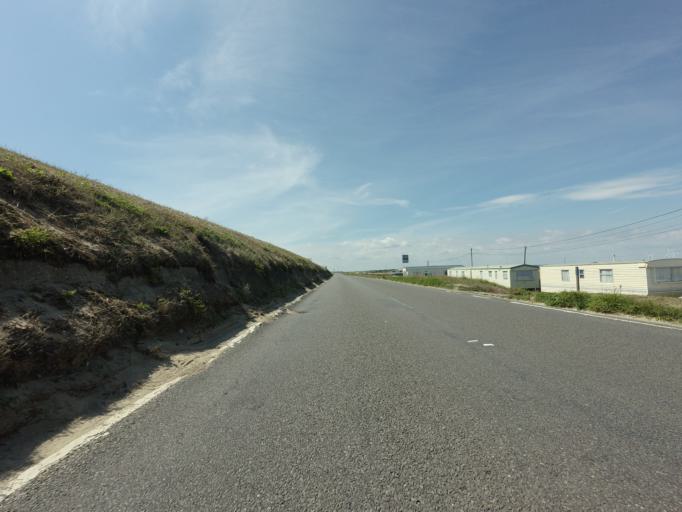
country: GB
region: England
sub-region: Kent
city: Lydd
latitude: 50.9286
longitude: 0.8240
